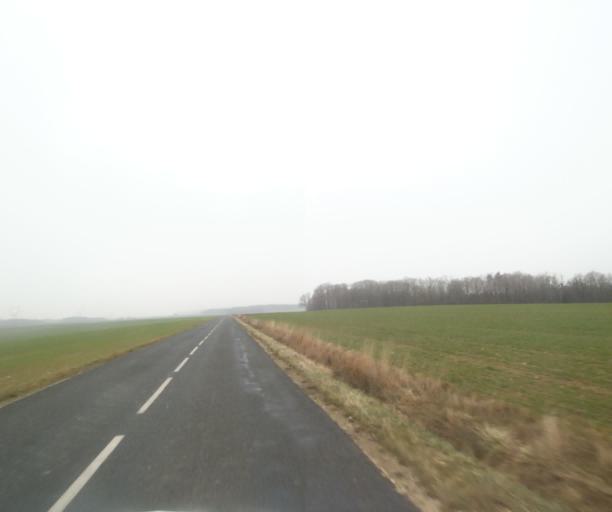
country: FR
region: Champagne-Ardenne
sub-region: Departement de la Haute-Marne
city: Bienville
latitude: 48.5211
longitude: 5.0650
